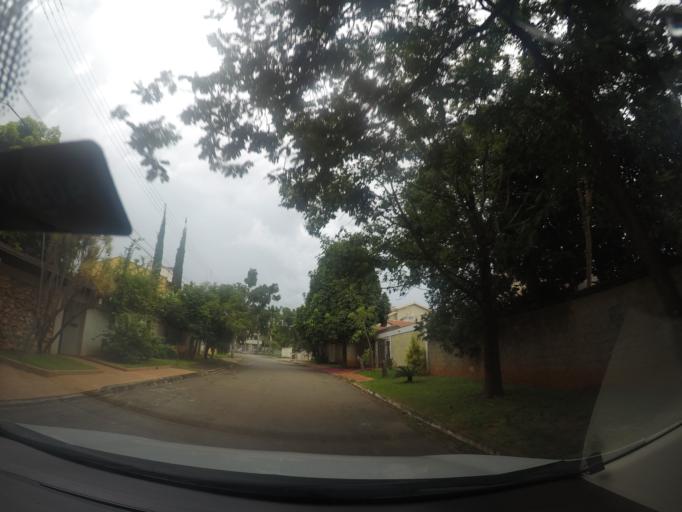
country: BR
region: Goias
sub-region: Goiania
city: Goiania
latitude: -16.6403
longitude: -49.2279
